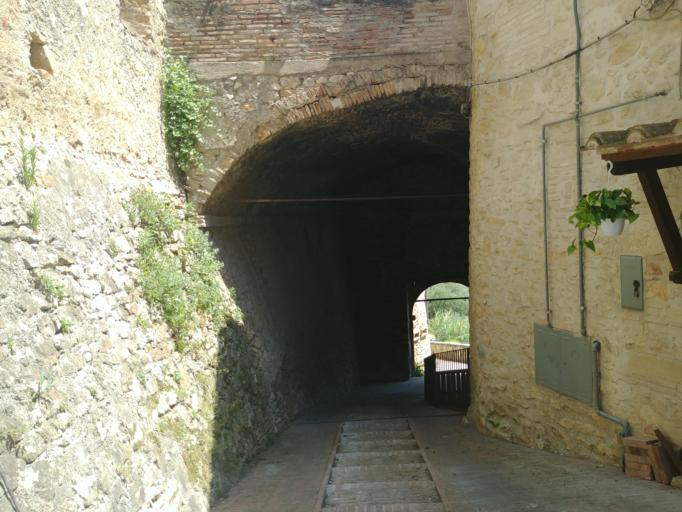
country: IT
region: Umbria
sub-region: Provincia di Terni
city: Fornole
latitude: 42.5045
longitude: 12.4690
